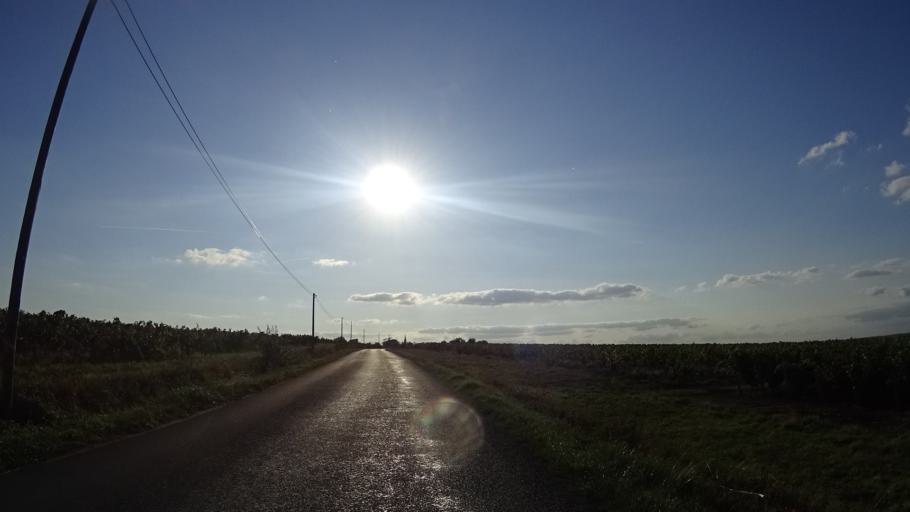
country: FR
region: Pays de la Loire
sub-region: Departement de Maine-et-Loire
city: Bouzille
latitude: 47.3413
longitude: -1.0938
